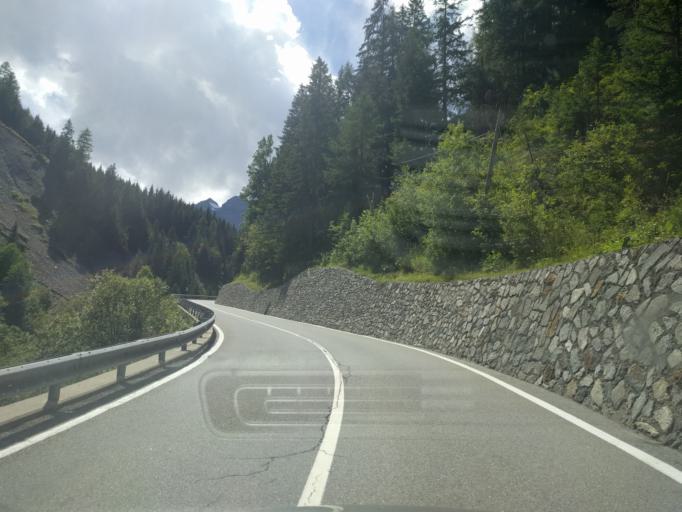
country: IT
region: Trentino-Alto Adige
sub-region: Bolzano
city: Stelvio
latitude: 46.5631
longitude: 10.5187
